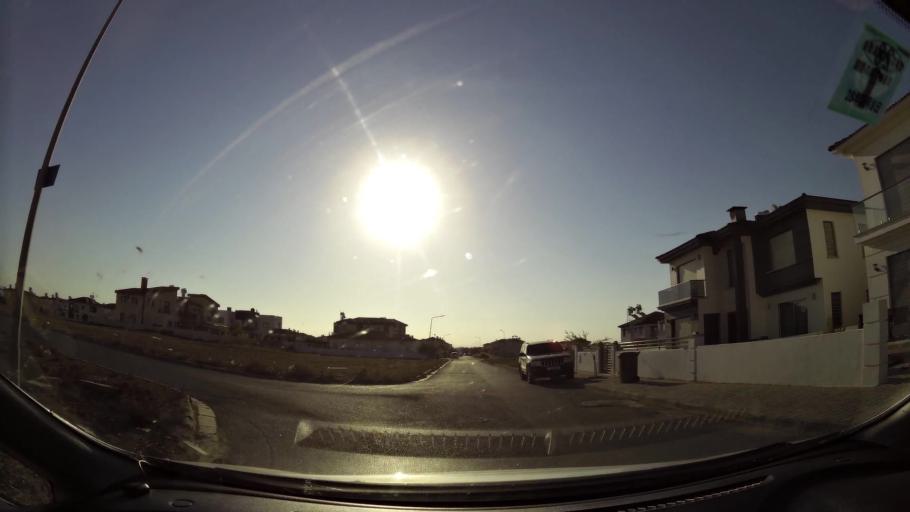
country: CY
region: Lefkosia
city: Nicosia
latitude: 35.2043
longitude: 33.2977
